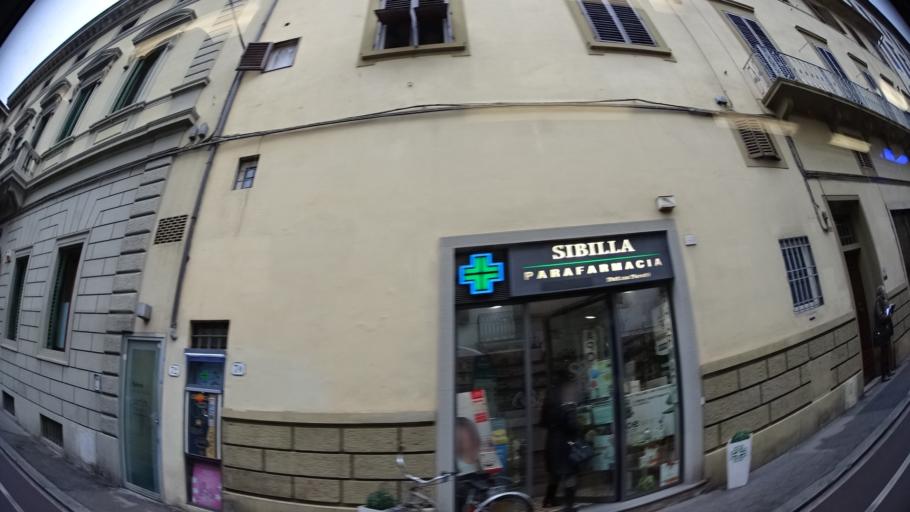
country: IT
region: Tuscany
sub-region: Province of Florence
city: Florence
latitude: 43.7813
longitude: 11.2620
